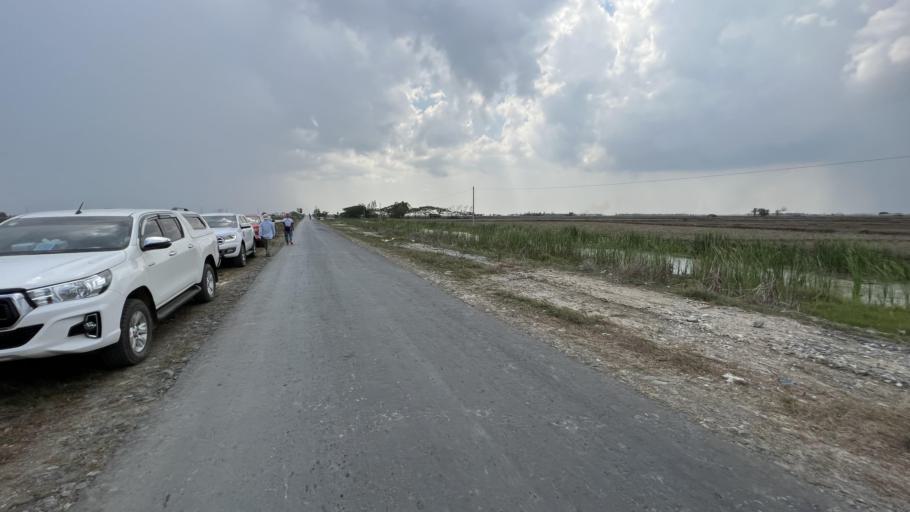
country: MM
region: Ayeyarwady
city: Pyapon
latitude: 16.0763
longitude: 95.6231
